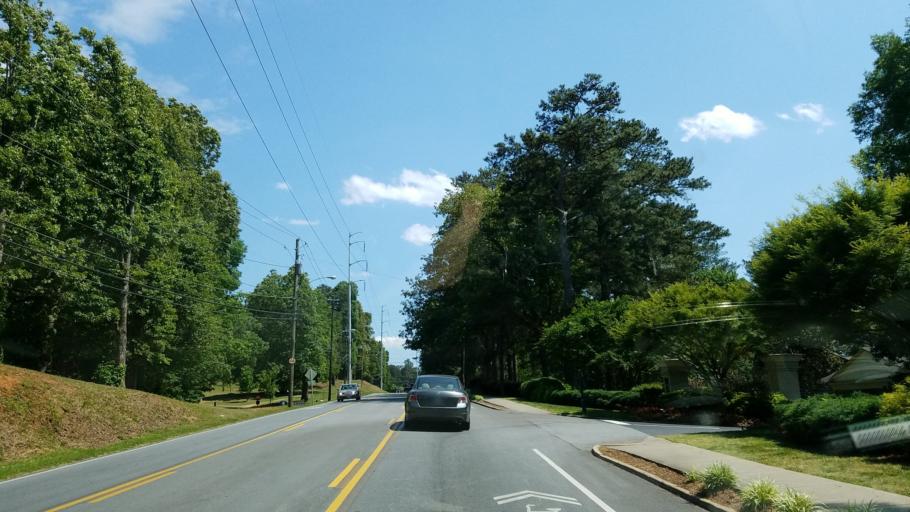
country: US
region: Georgia
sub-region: DeKalb County
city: Chamblee
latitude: 33.8985
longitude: -84.3310
